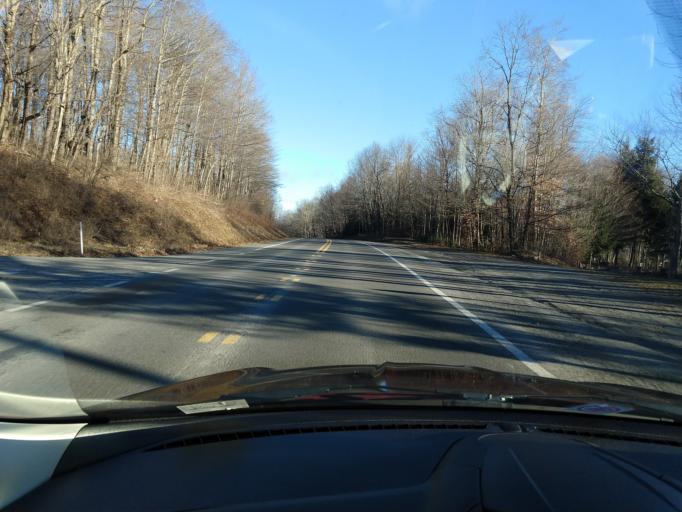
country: US
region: Virginia
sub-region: Highland County
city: Monterey
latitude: 38.5690
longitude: -79.8412
